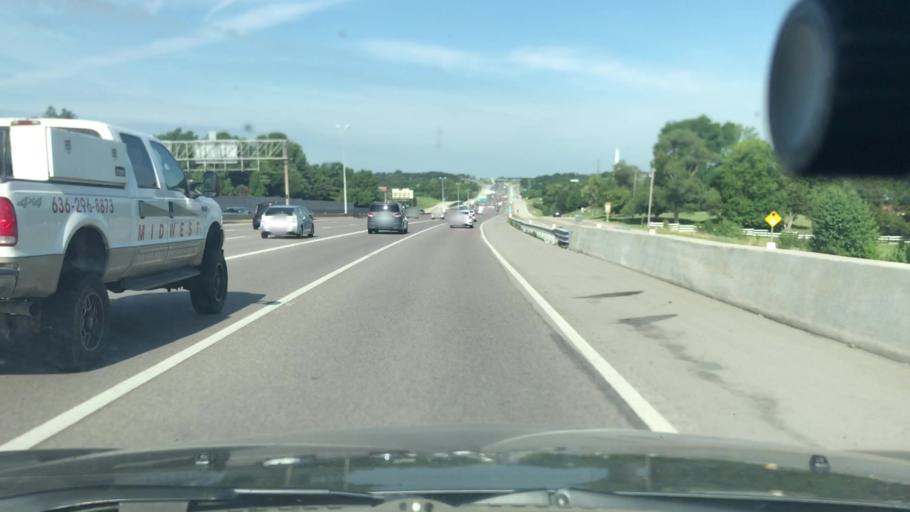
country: US
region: Missouri
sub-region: Saint Louis County
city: Town and Country
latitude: 38.6390
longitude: -90.4554
